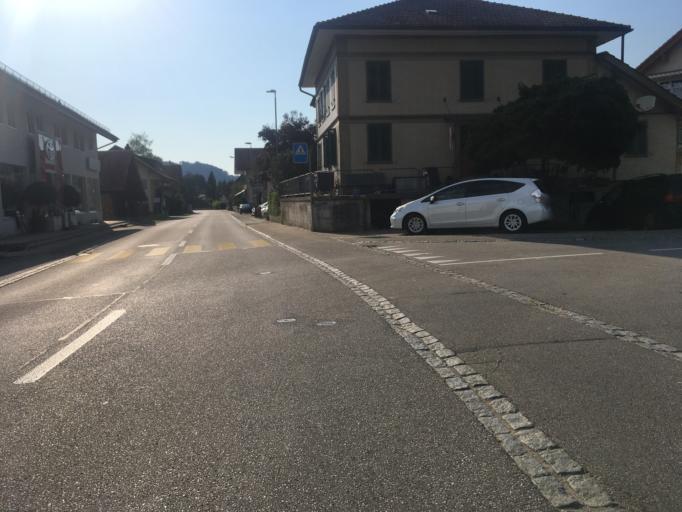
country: CH
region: Bern
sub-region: Emmental District
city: Lutzelfluh
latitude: 47.0155
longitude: 7.6656
